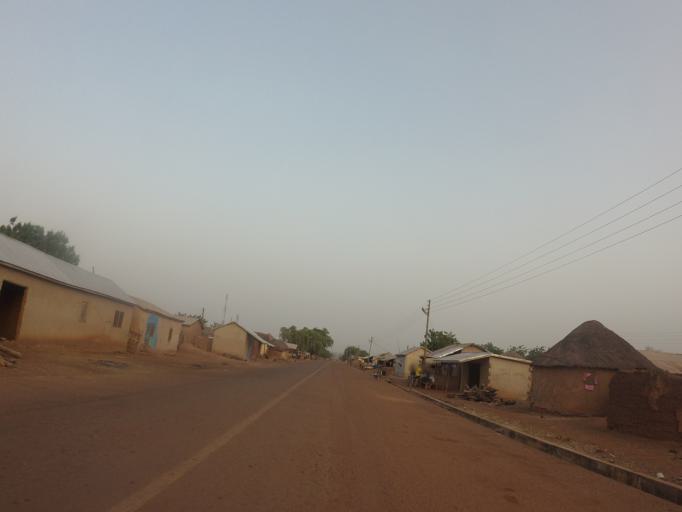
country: GH
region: Northern
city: Tamale
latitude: 9.4453
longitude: -1.1169
